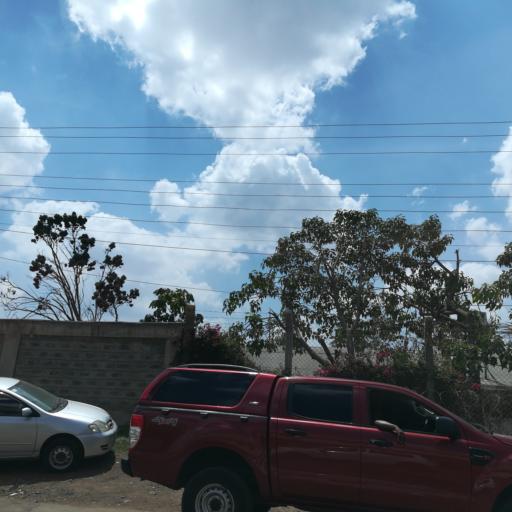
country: KE
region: Nairobi Area
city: Nairobi
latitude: -1.3184
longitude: 36.8156
